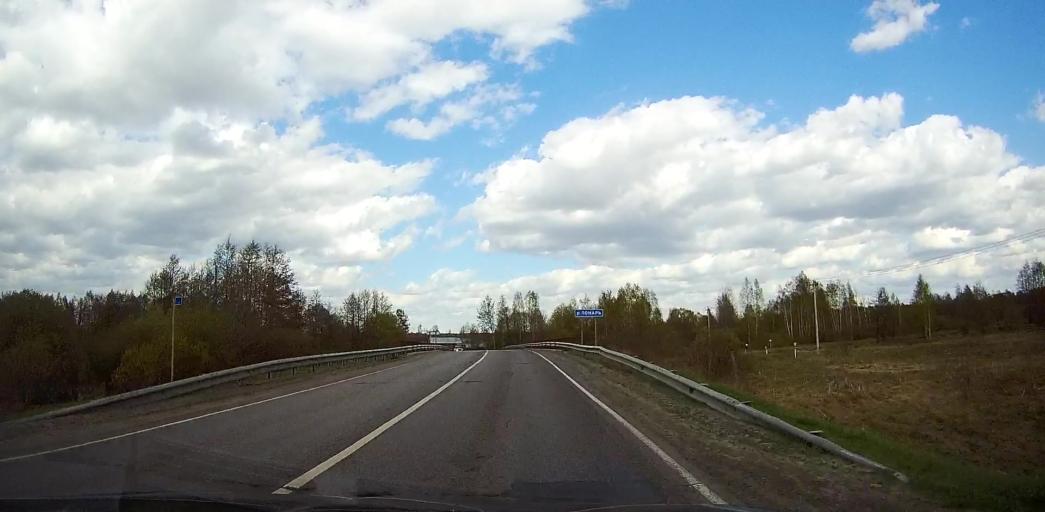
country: RU
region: Moskovskaya
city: Davydovo
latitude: 55.6319
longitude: 38.8674
